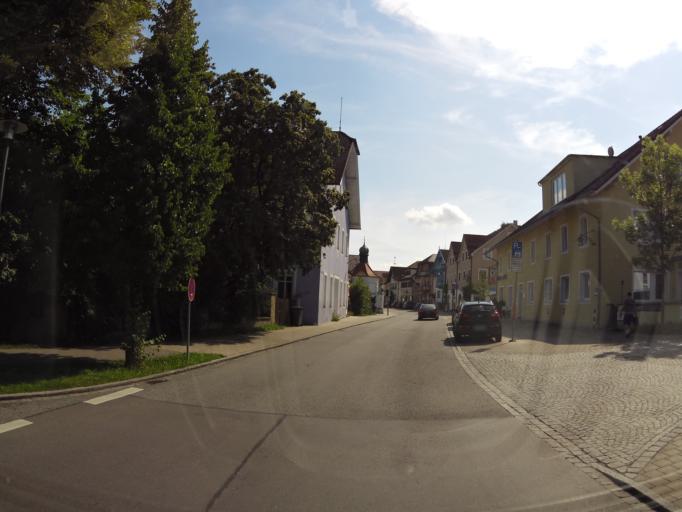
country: DE
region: Bavaria
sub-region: Upper Bavaria
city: Diessen am Ammersee
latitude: 47.9502
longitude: 11.1034
